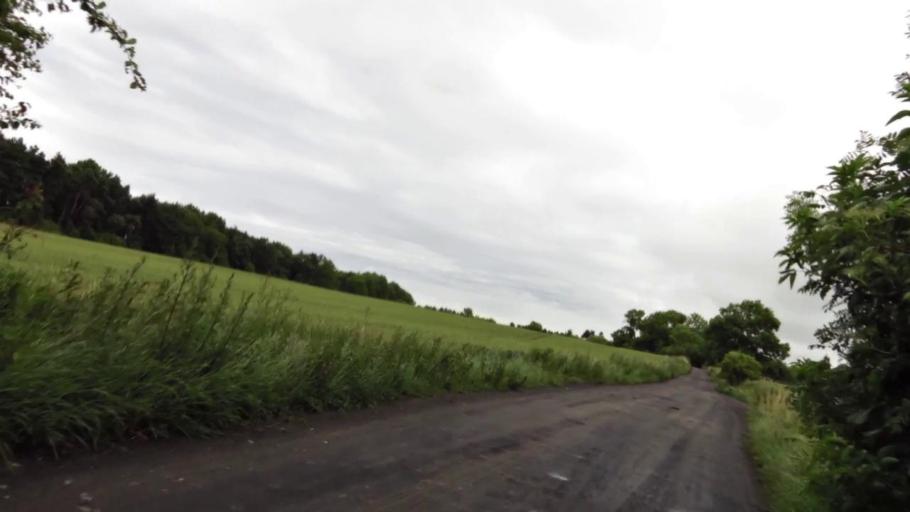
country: PL
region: West Pomeranian Voivodeship
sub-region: Powiat koszalinski
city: Mielno
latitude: 54.2456
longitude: 15.9259
